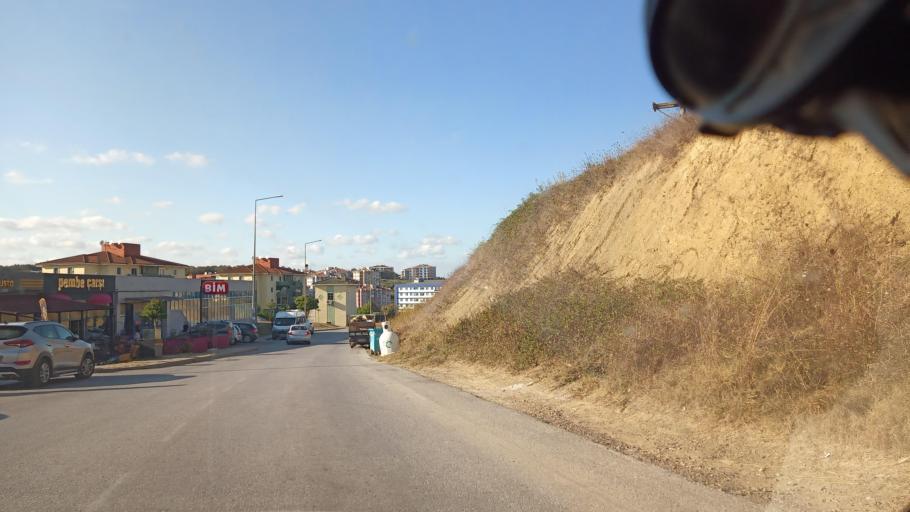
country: TR
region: Sakarya
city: Kazimpasa
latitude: 40.8553
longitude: 30.2774
